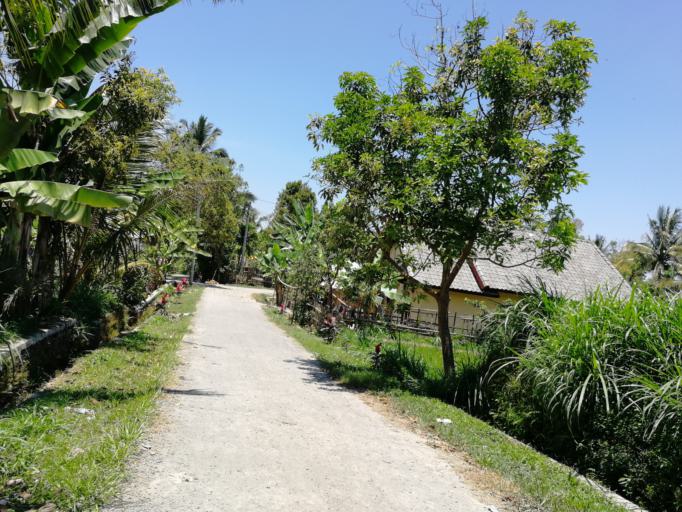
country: ID
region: West Nusa Tenggara
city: Tetebatu
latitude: -8.5449
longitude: 116.4211
